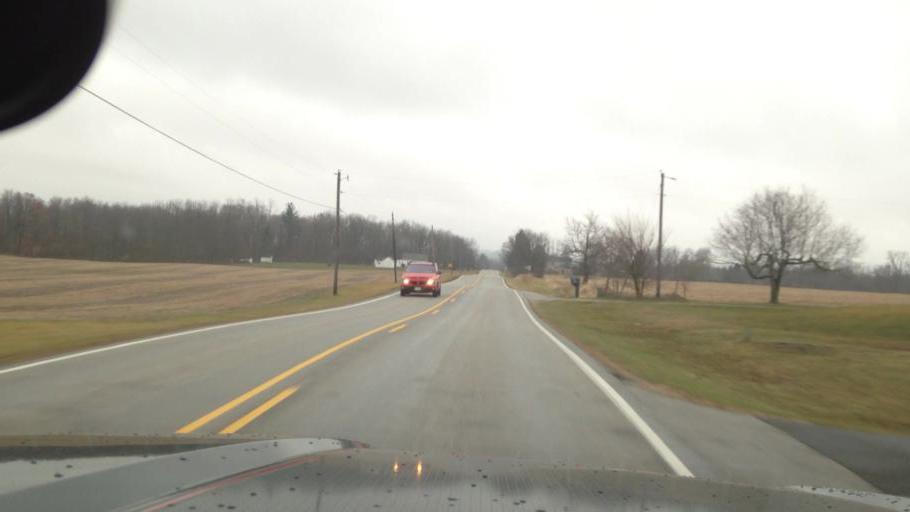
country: US
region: Ohio
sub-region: Preble County
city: New Paris
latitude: 39.9059
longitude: -84.8318
